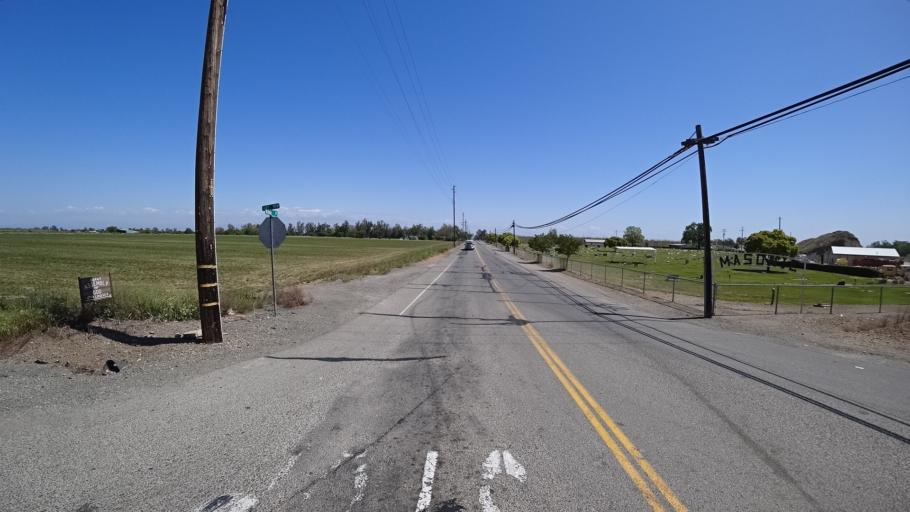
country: US
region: California
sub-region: Glenn County
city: Orland
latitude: 39.7690
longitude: -122.1966
